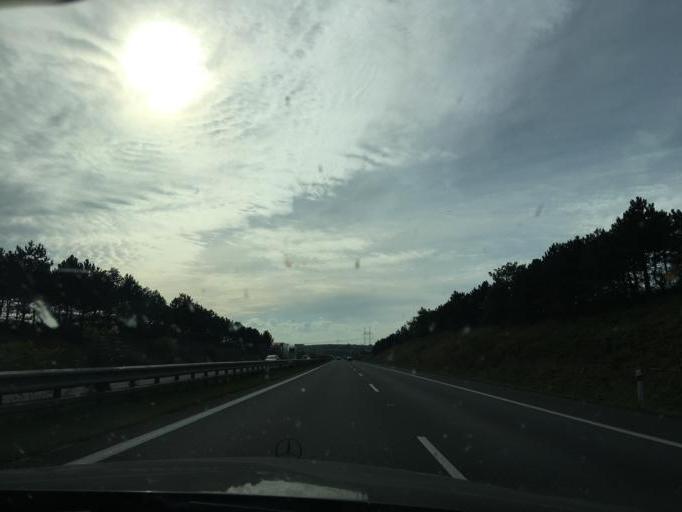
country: CZ
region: Central Bohemia
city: Prerov nad Labem
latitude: 50.1363
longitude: 14.8267
